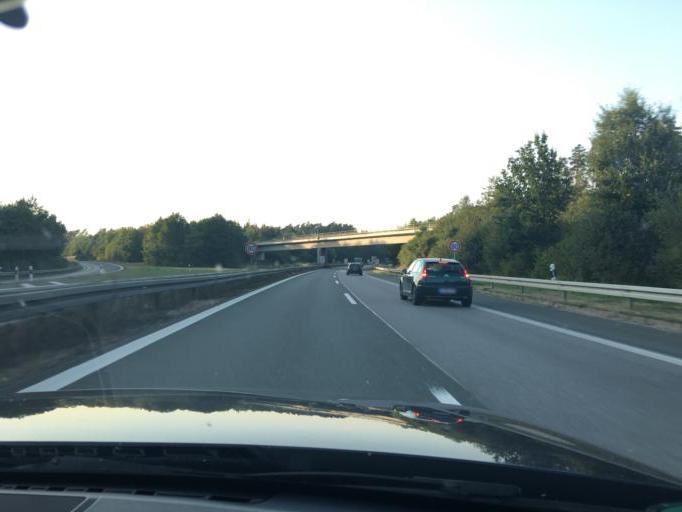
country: DE
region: Bavaria
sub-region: Upper Franconia
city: Strullendorf
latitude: 49.8694
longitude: 10.9515
